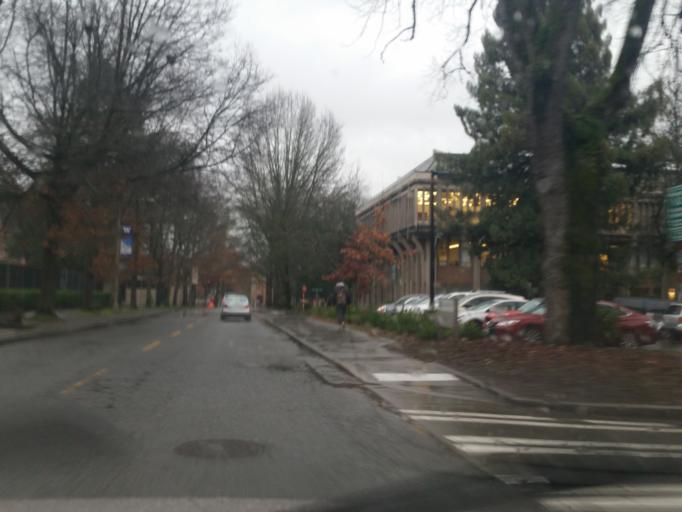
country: US
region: Washington
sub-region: King County
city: Seattle
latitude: 47.6593
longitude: -122.3069
